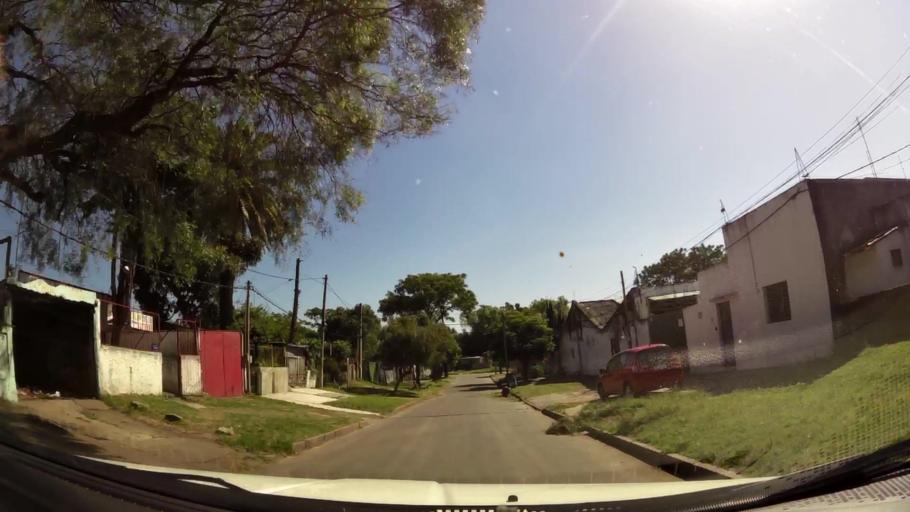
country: UY
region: Montevideo
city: Montevideo
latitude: -34.8540
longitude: -56.2387
